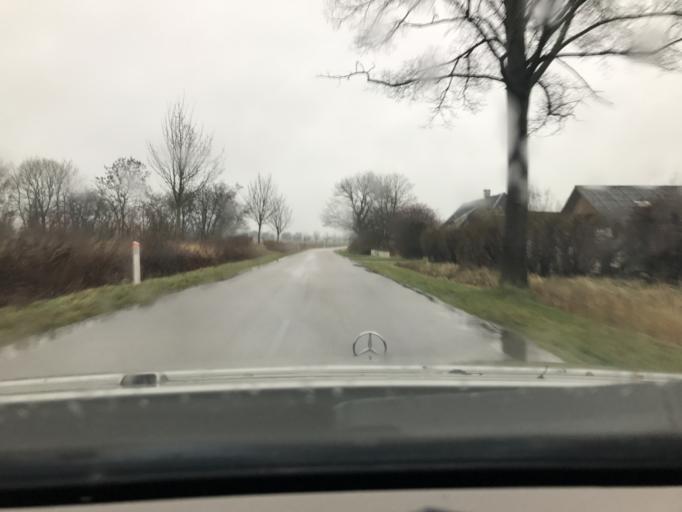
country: DK
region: South Denmark
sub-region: Sonderborg Kommune
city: Horuphav
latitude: 54.8864
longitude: 10.0013
